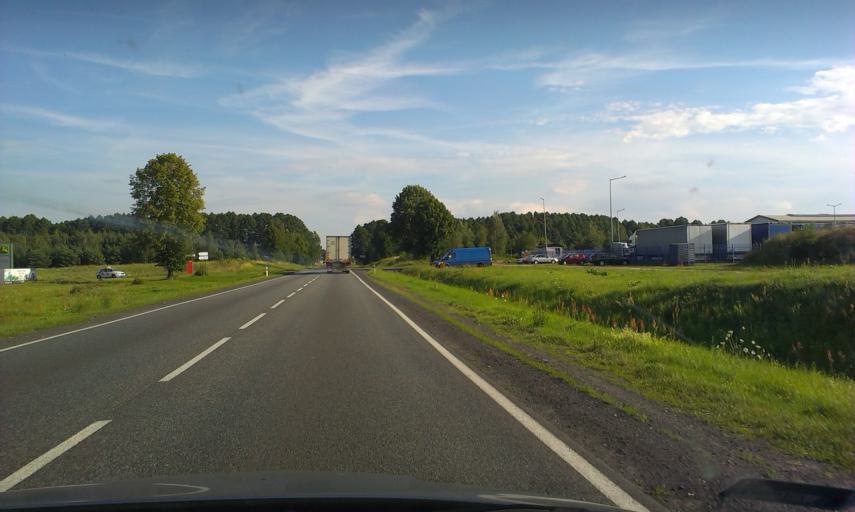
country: PL
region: Kujawsko-Pomorskie
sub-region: Powiat bydgoski
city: Biale Blota
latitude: 53.1319
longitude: 17.8801
